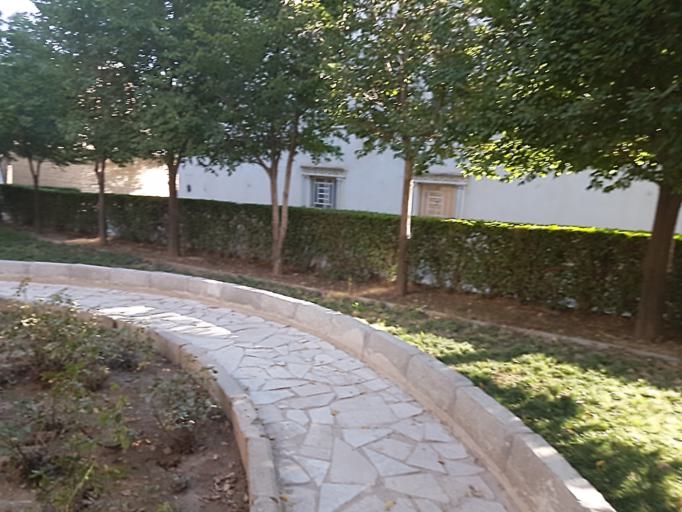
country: IR
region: Markazi
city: Arak
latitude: 34.0660
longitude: 49.6825
